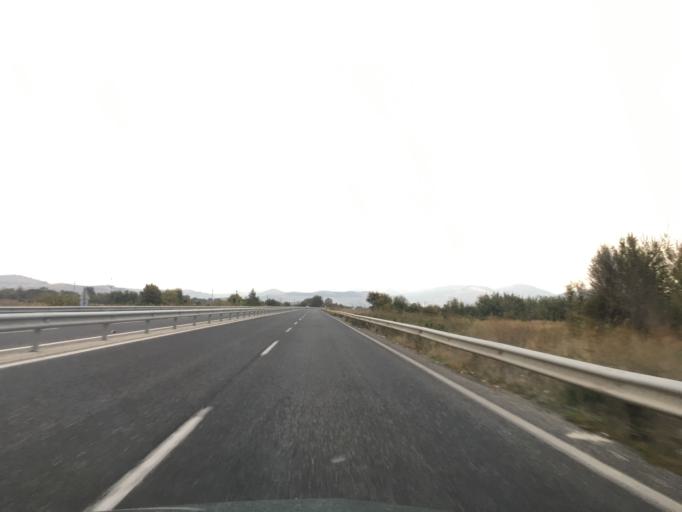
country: GR
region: Thessaly
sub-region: Trikala
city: Trikala
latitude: 39.5592
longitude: 21.8022
